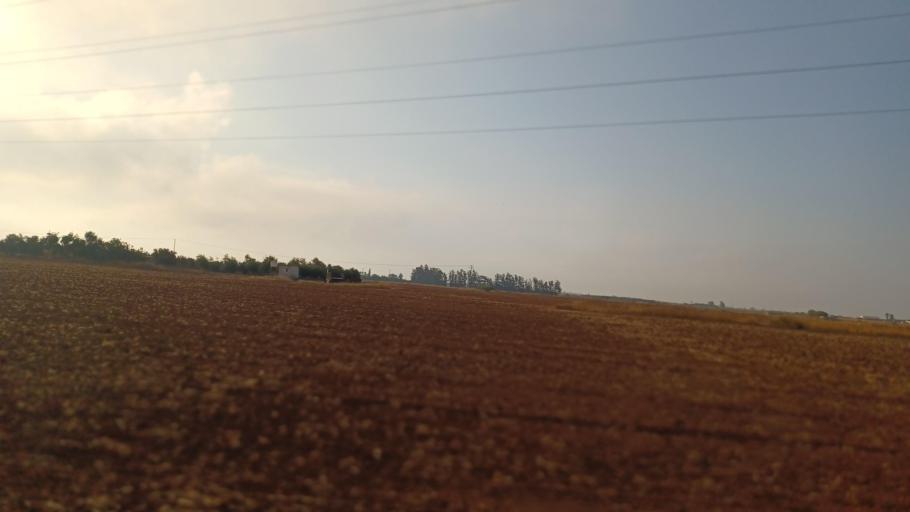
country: CY
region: Ammochostos
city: Avgorou
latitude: 35.0410
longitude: 33.8666
